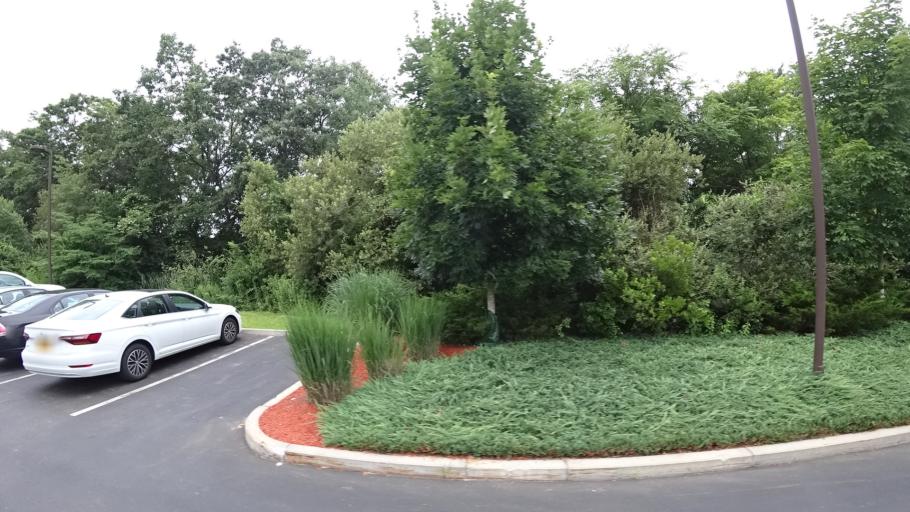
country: US
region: Massachusetts
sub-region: Norfolk County
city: Dedham
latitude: 42.2254
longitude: -71.1722
